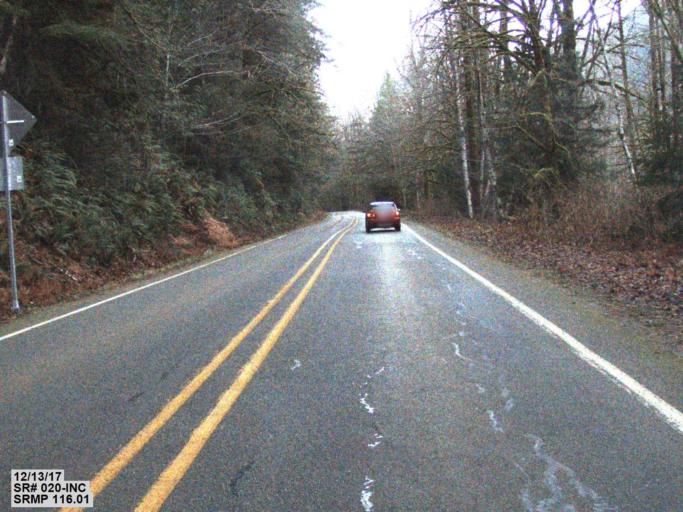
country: US
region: Washington
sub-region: Snohomish County
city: Darrington
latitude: 48.6359
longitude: -121.3200
